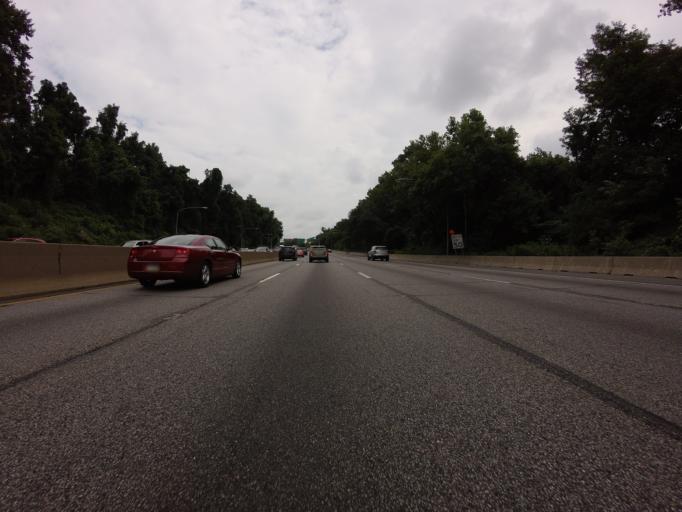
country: US
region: Pennsylvania
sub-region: Montgomery County
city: Bala-Cynwyd
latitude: 39.9968
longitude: -75.1966
